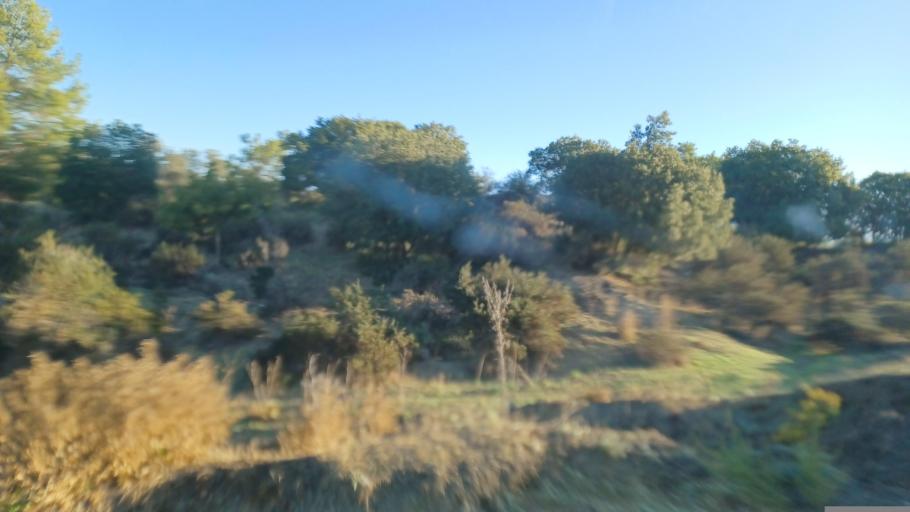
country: CY
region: Pafos
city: Polis
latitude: 34.9458
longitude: 32.5618
